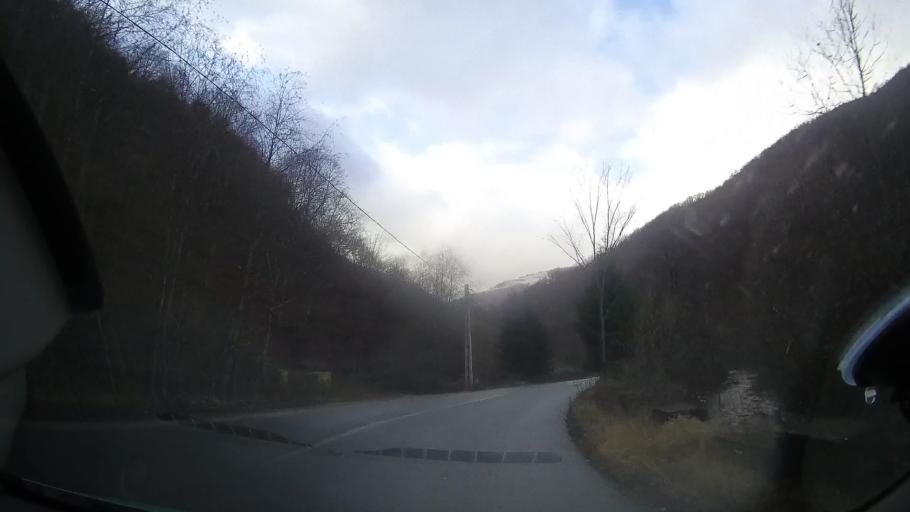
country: RO
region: Cluj
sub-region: Comuna Maguri-Racatau
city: Maguri-Racatau
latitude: 46.6670
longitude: 23.2461
